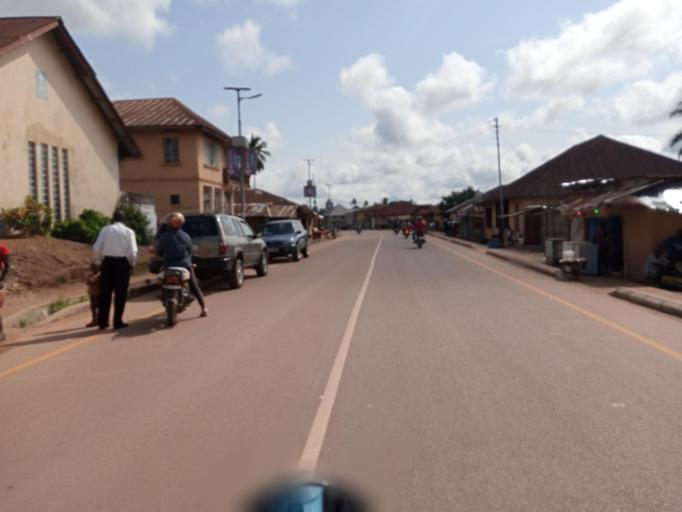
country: SL
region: Southern Province
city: Bo
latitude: 7.9701
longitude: -11.7386
